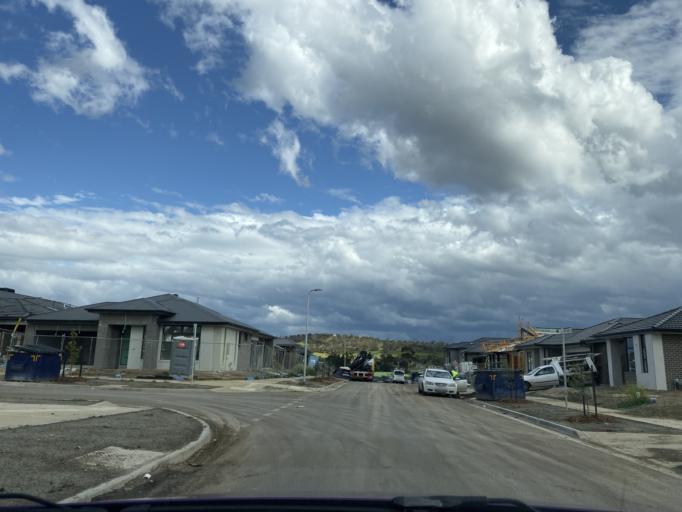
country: AU
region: Victoria
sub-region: Whittlesea
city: Mernda
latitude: -37.5964
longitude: 145.0750
